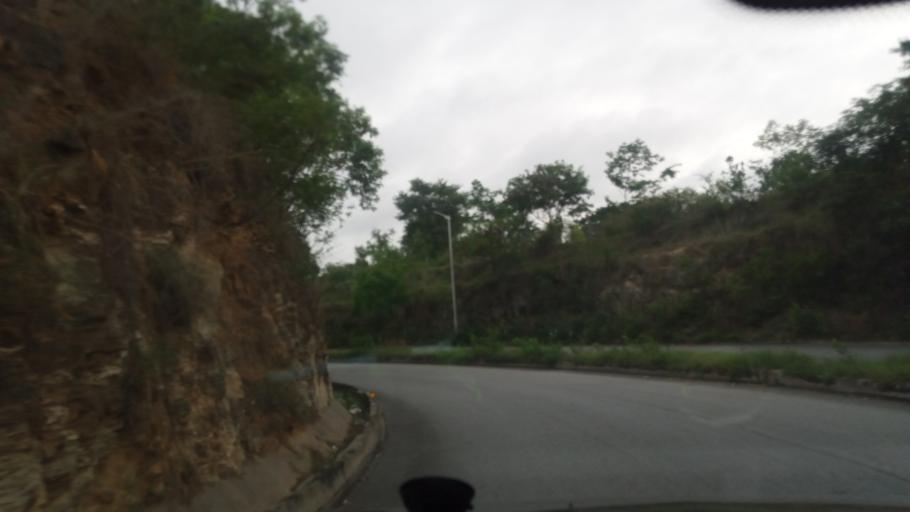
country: IN
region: Karnataka
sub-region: Bangalore Urban
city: Bangalore
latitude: 12.9008
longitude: 77.4724
